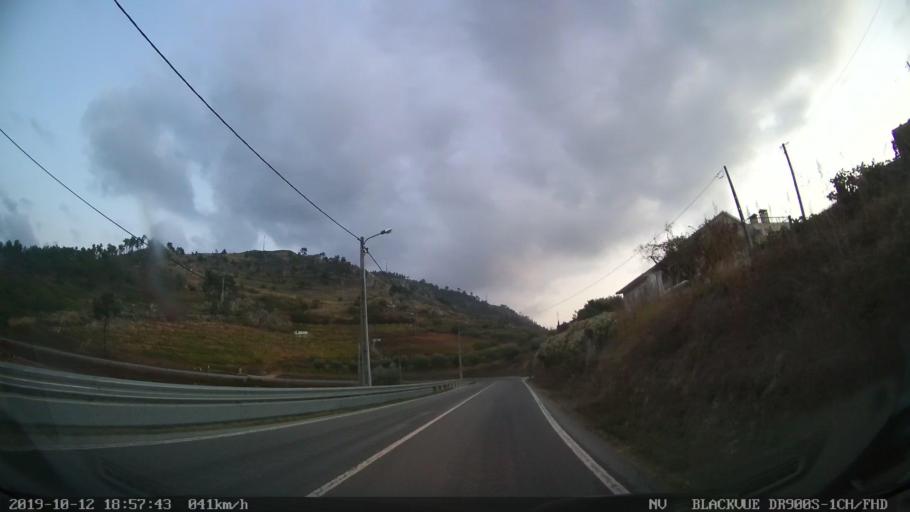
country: PT
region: Vila Real
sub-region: Peso da Regua
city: Peso da Regua
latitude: 41.1306
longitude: -7.7506
